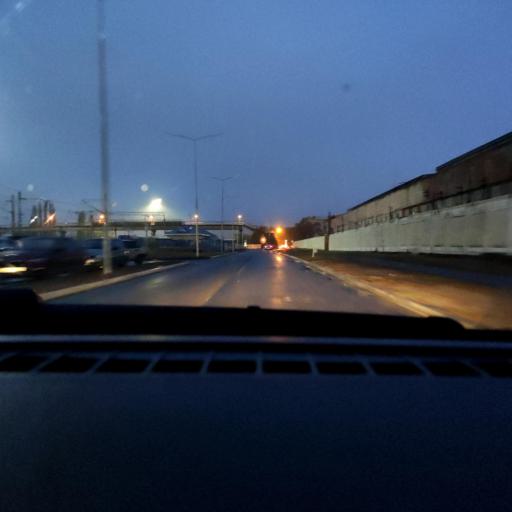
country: RU
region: Voronezj
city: Voronezh
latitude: 51.6376
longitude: 39.2570
